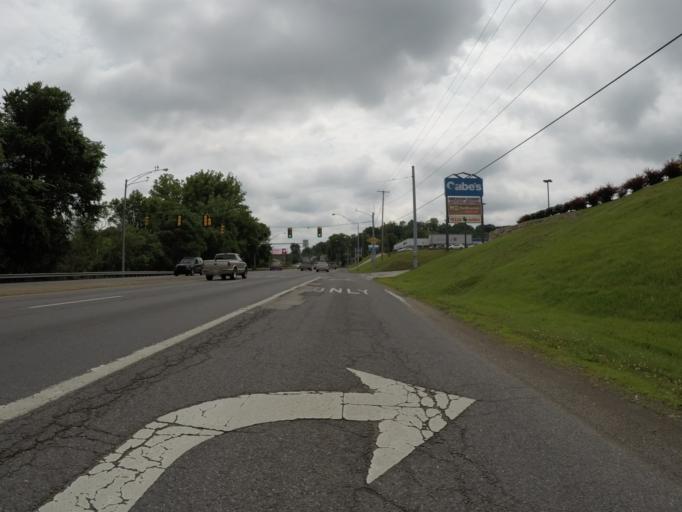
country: US
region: West Virginia
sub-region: Cabell County
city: Huntington
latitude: 38.4114
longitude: -82.3856
